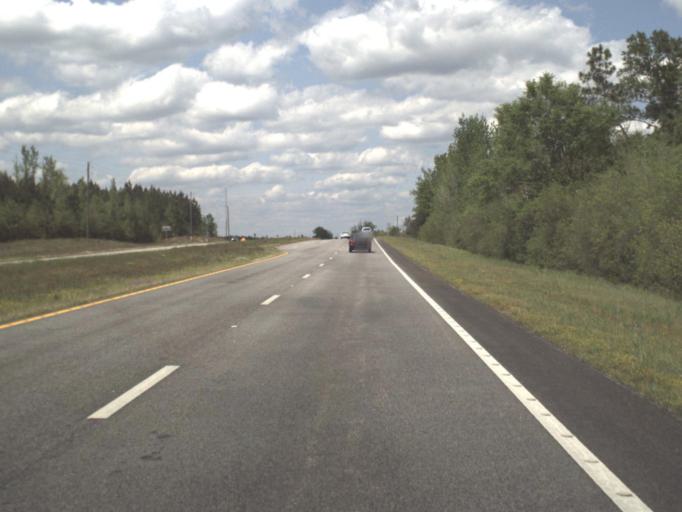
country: US
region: Florida
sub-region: Escambia County
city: Molino
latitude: 30.7861
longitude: -87.3346
